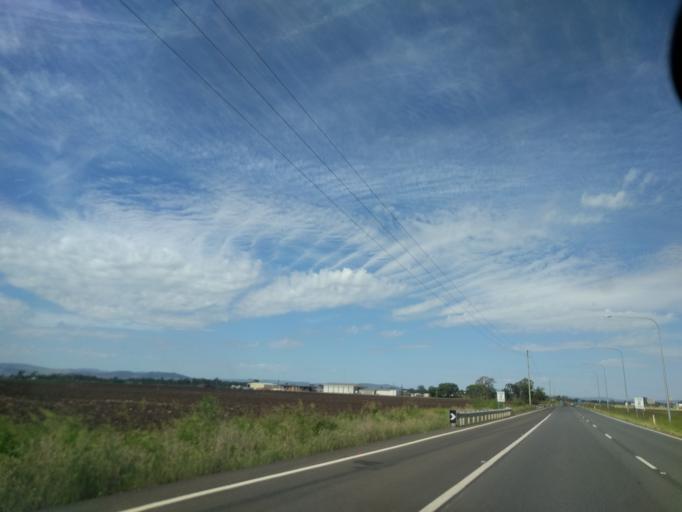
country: AU
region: Queensland
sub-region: Lockyer Valley
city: Gatton
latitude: -27.5423
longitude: 152.3571
